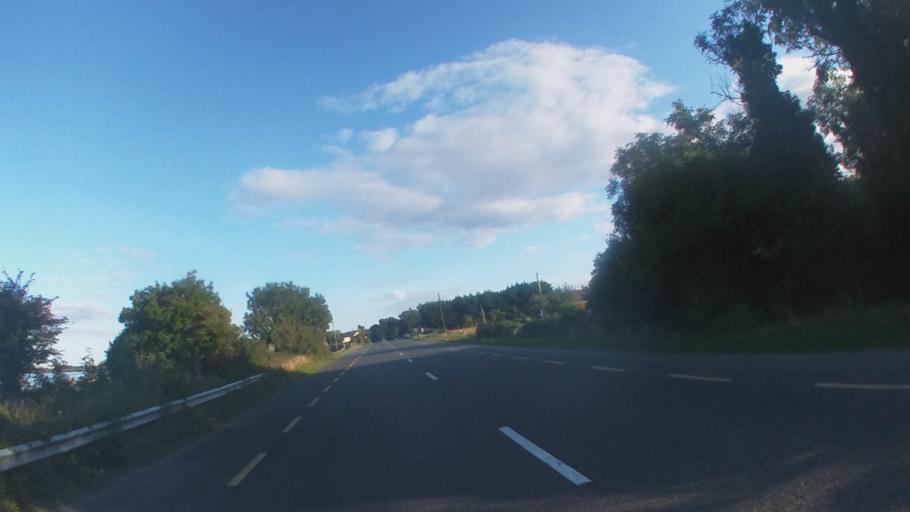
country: IE
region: Leinster
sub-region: Lu
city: Carlingford
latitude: 54.0305
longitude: -6.1578
